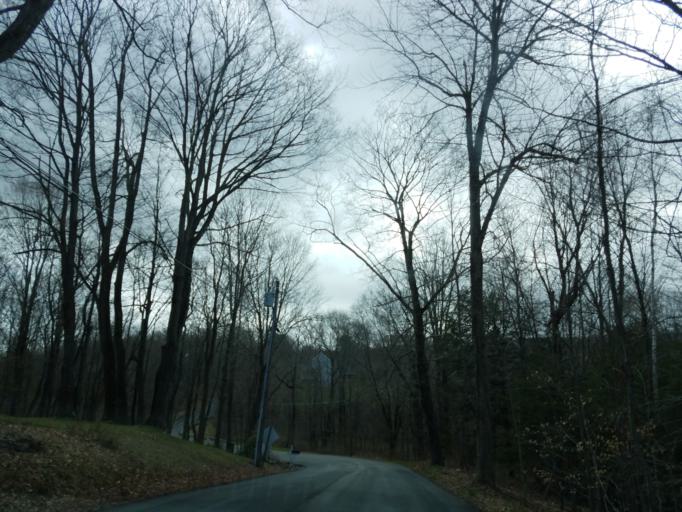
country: US
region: Connecticut
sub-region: Litchfield County
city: West Torrington
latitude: 41.7835
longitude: -73.1648
